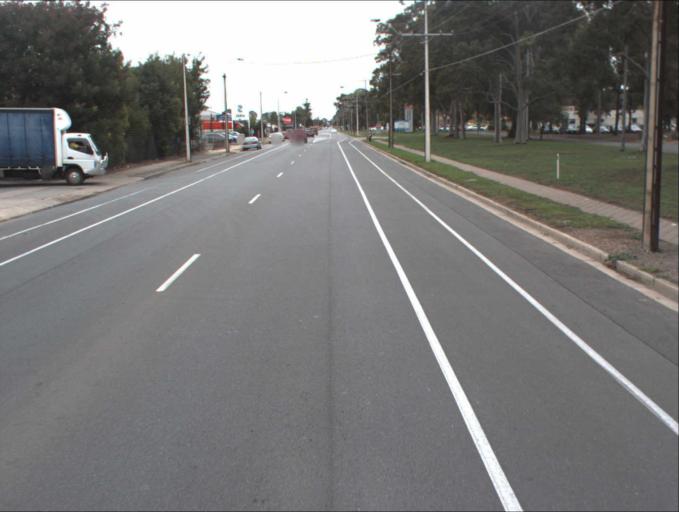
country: AU
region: South Australia
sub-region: Charles Sturt
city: Woodville
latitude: -34.8741
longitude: 138.5662
